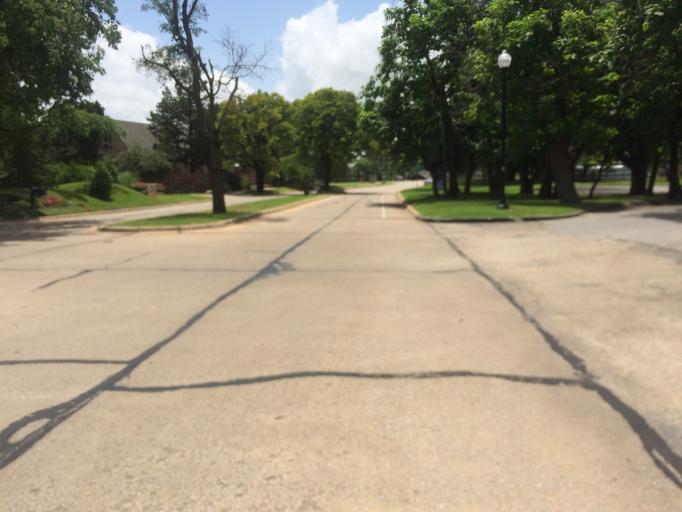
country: US
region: Oklahoma
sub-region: Cleveland County
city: Norman
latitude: 35.1951
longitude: -97.4687
